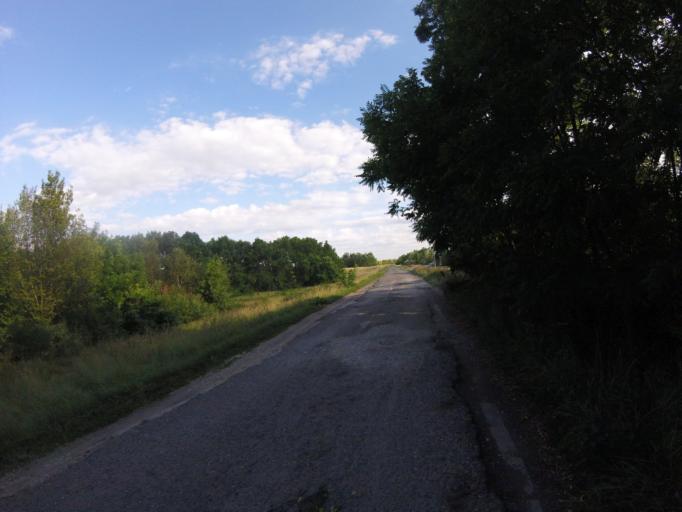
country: HU
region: Heves
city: Poroszlo
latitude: 47.6348
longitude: 20.6417
